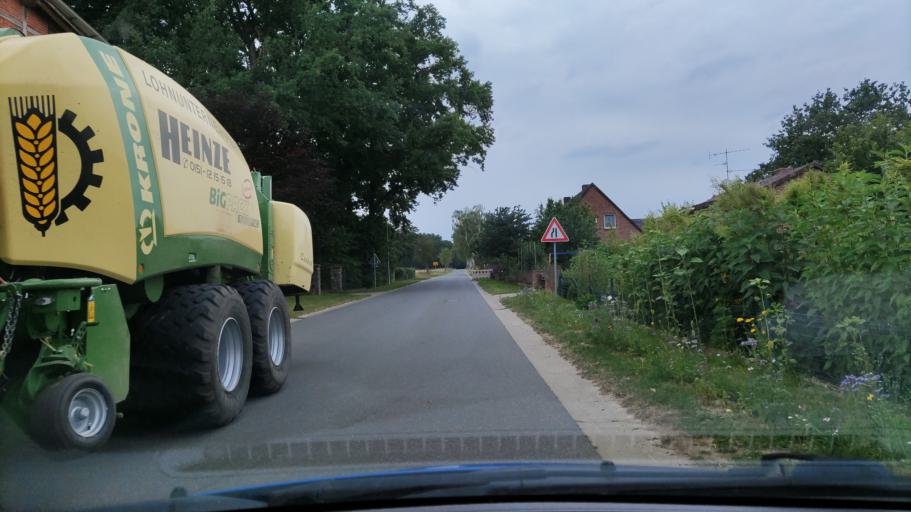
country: DE
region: Lower Saxony
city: Suhlendorf
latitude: 52.9669
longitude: 10.8301
